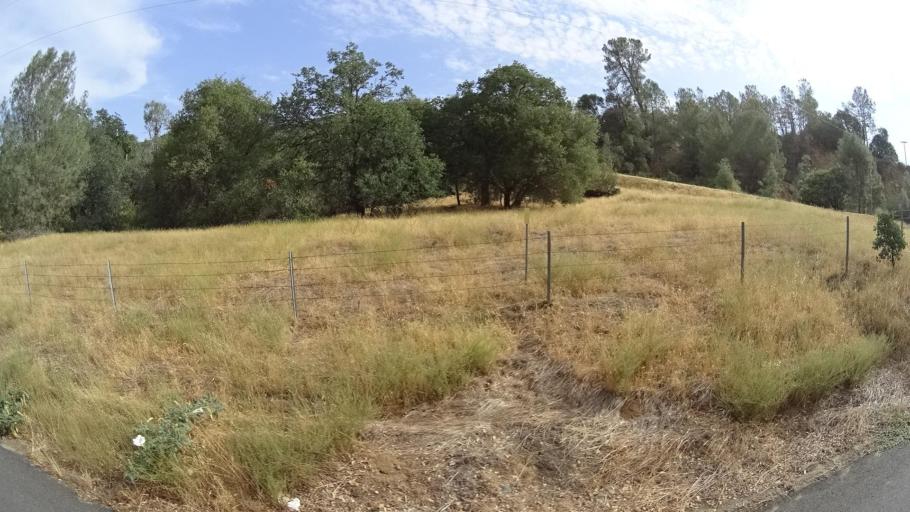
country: US
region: California
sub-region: Mariposa County
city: Midpines
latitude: 37.5084
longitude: -119.8633
